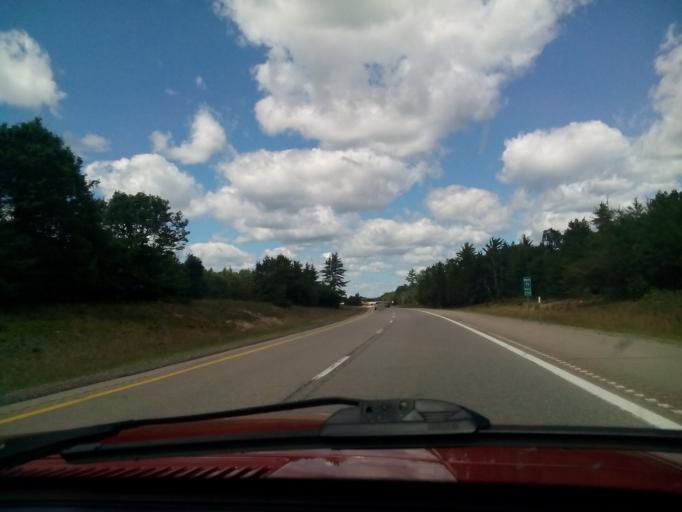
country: US
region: Michigan
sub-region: Crawford County
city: Grayling
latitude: 44.6606
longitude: -84.6974
